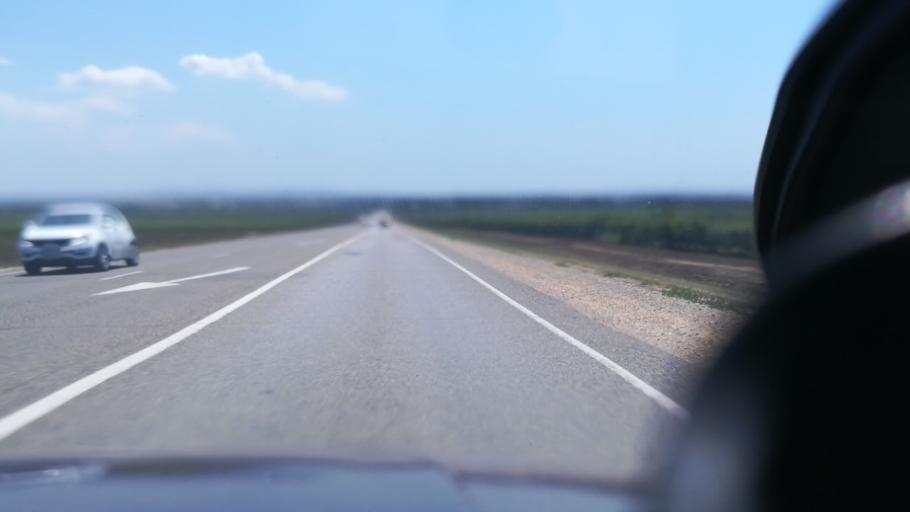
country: RU
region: Krasnodarskiy
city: Vinogradnyy
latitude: 45.0809
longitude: 37.3179
